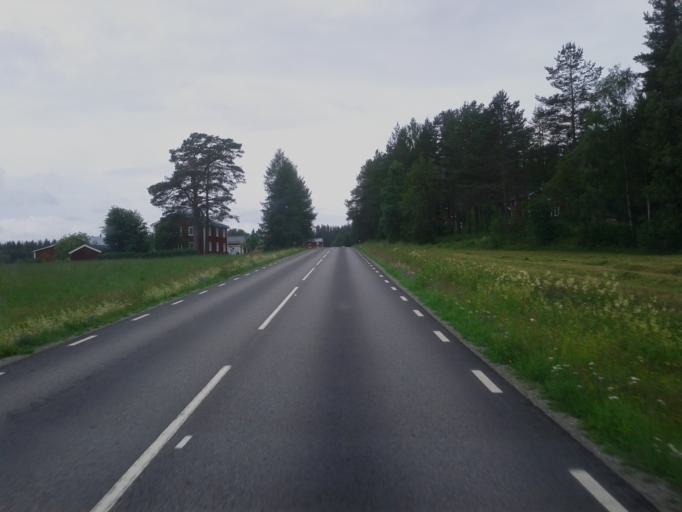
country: SE
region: Vaesterbotten
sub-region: Skelleftea Kommun
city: Viken
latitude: 64.8844
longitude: 20.7662
